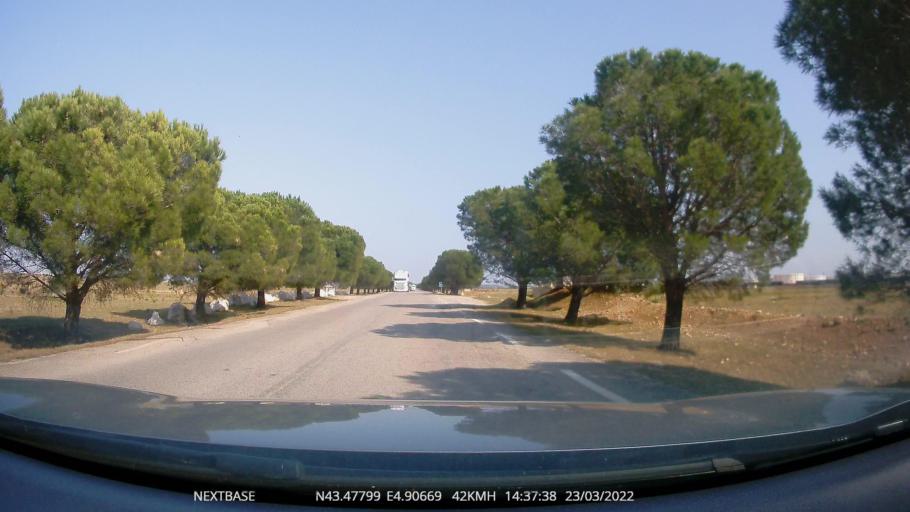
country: FR
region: Provence-Alpes-Cote d'Azur
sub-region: Departement des Bouches-du-Rhone
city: Fos-sur-Mer
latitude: 43.4780
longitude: 4.9067
